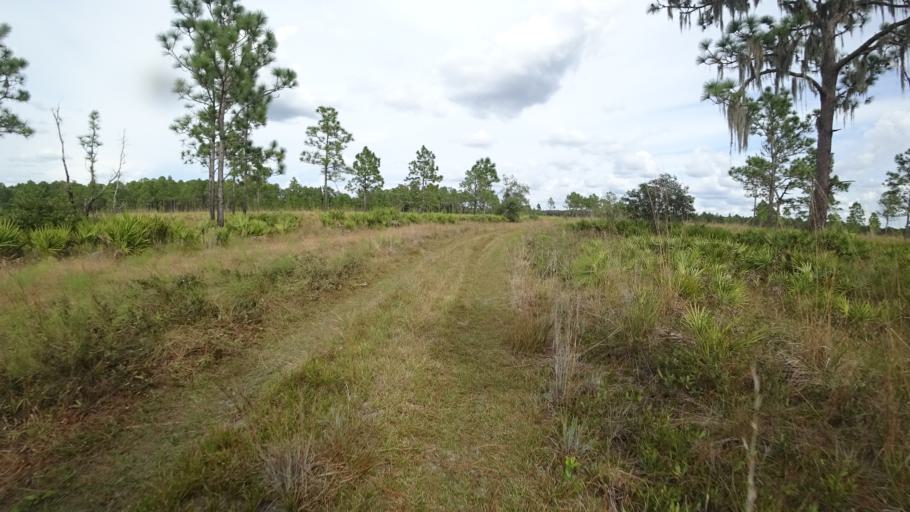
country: US
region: Florida
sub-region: Hillsborough County
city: Wimauma
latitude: 27.5650
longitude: -82.1400
